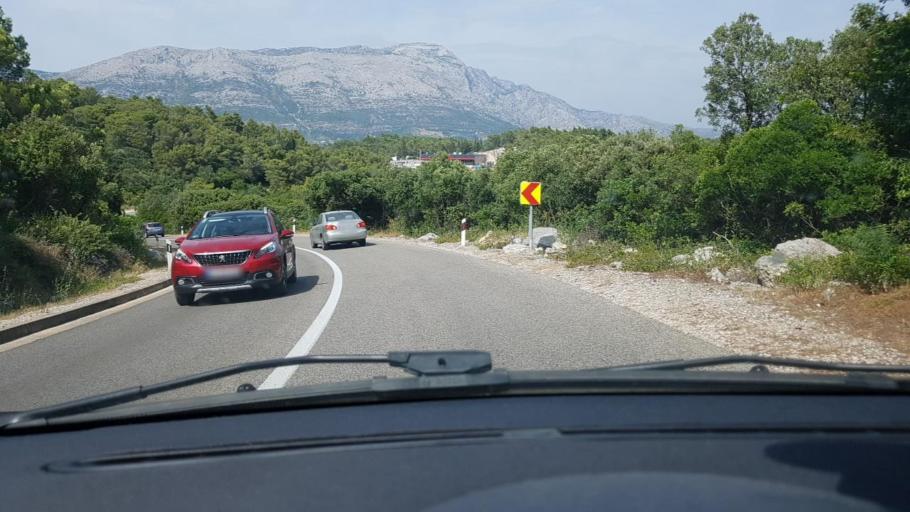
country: HR
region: Dubrovacko-Neretvanska
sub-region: Grad Korcula
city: Zrnovo
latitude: 42.9498
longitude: 17.1240
